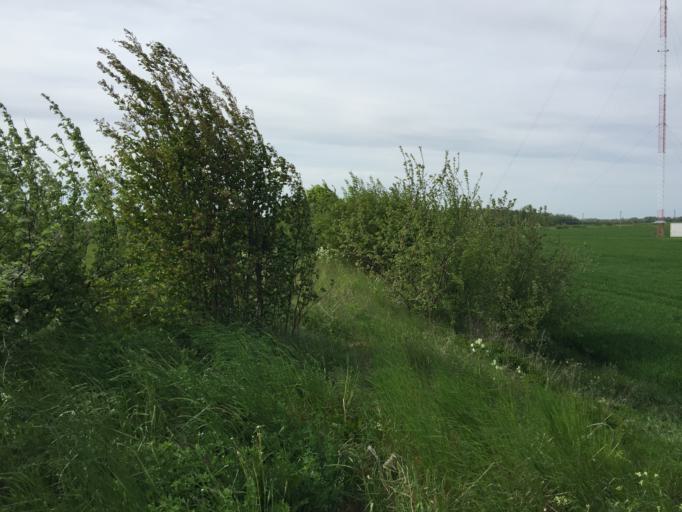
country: LT
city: Linkuva
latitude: 56.0250
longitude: 24.1849
